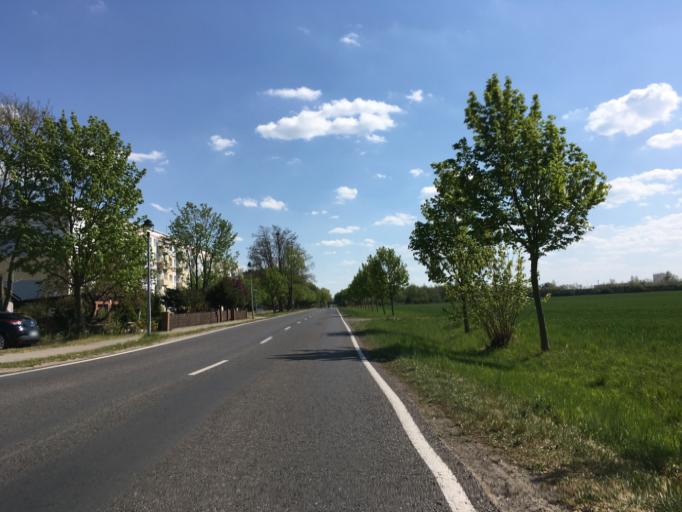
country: DE
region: Brandenburg
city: Werneuchen
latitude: 52.6153
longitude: 13.6782
